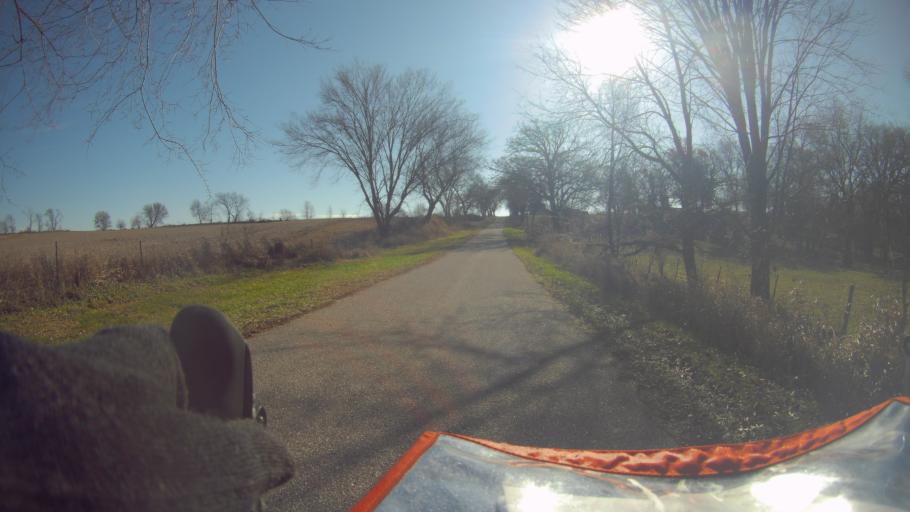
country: US
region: Wisconsin
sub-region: Rock County
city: Evansville
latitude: 42.8452
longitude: -89.2798
